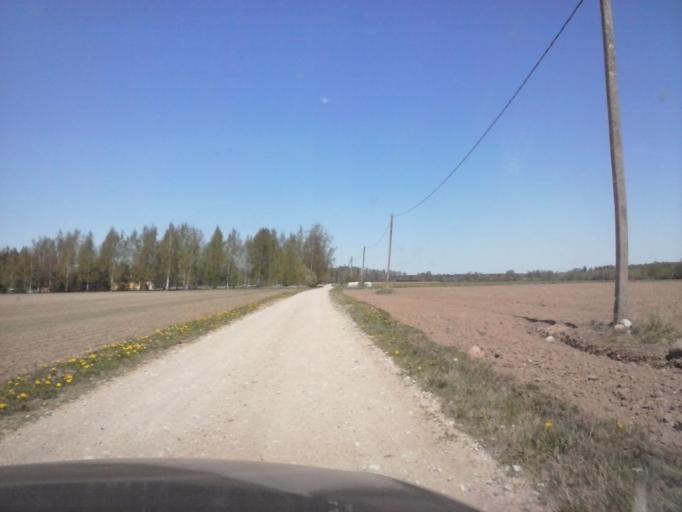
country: EE
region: Valgamaa
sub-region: Torva linn
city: Torva
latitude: 58.2247
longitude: 25.8978
